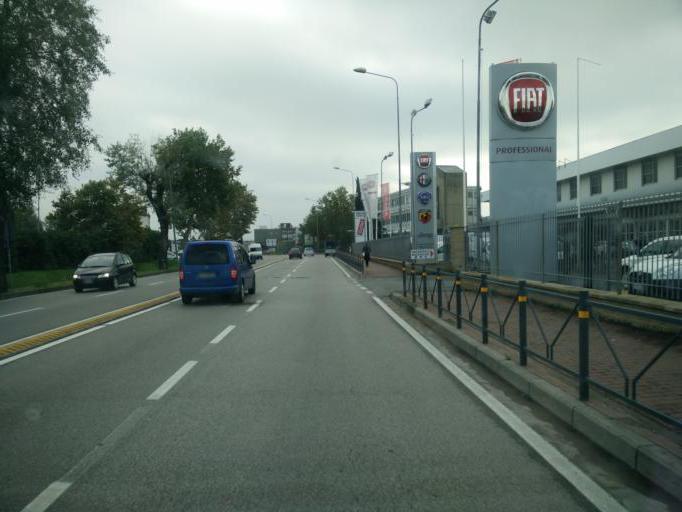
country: IT
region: Tuscany
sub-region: Province of Florence
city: Mantignano-Ugnano
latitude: 43.8048
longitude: 11.1818
